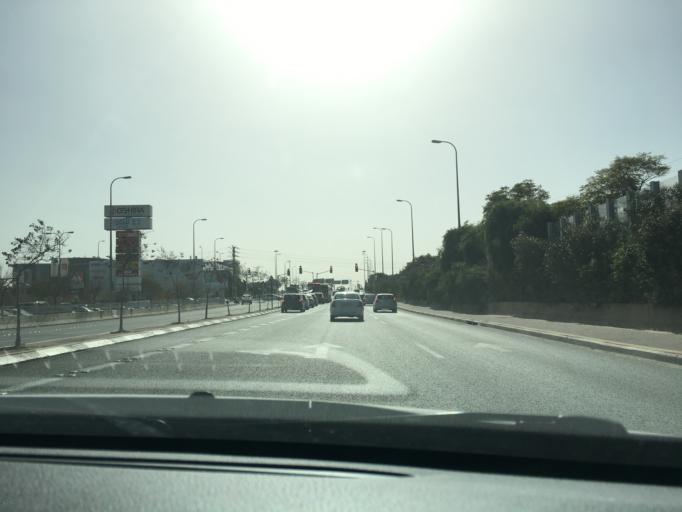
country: IL
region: Central District
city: Kfar Saba
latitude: 32.1681
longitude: 34.9281
